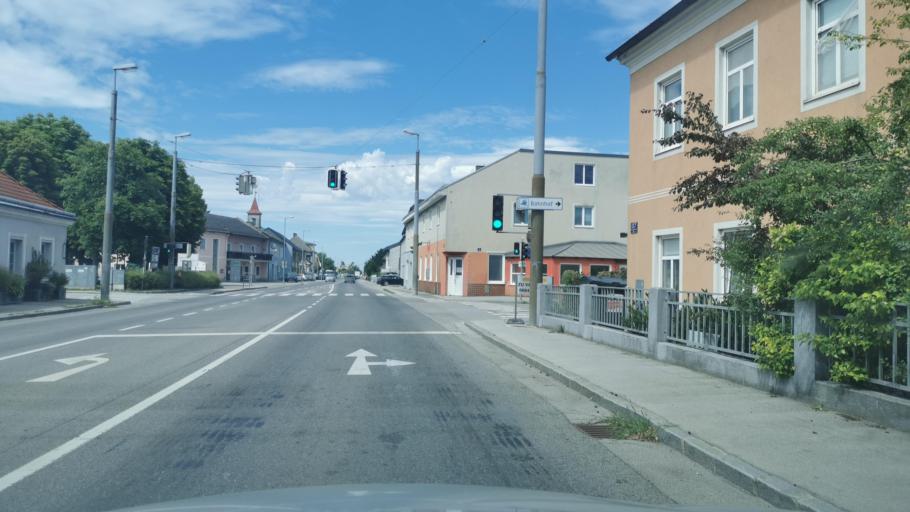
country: AT
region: Lower Austria
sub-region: Politischer Bezirk Sankt Polten
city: Wilhelmsburg
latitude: 48.1380
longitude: 15.6133
